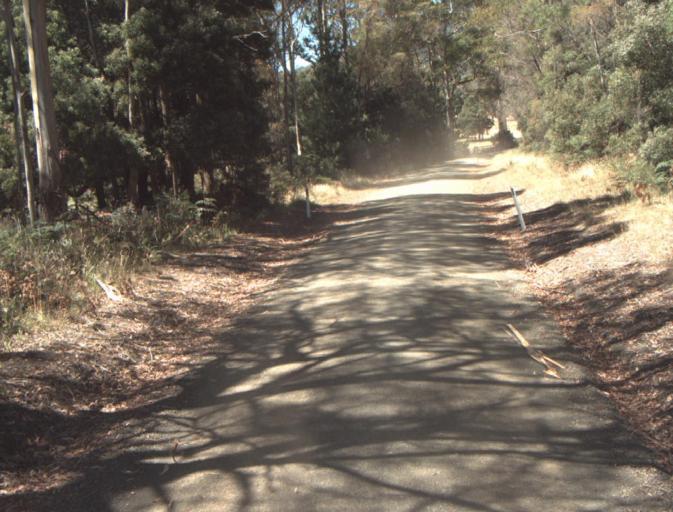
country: AU
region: Tasmania
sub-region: Launceston
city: Newstead
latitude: -41.3423
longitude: 147.3672
